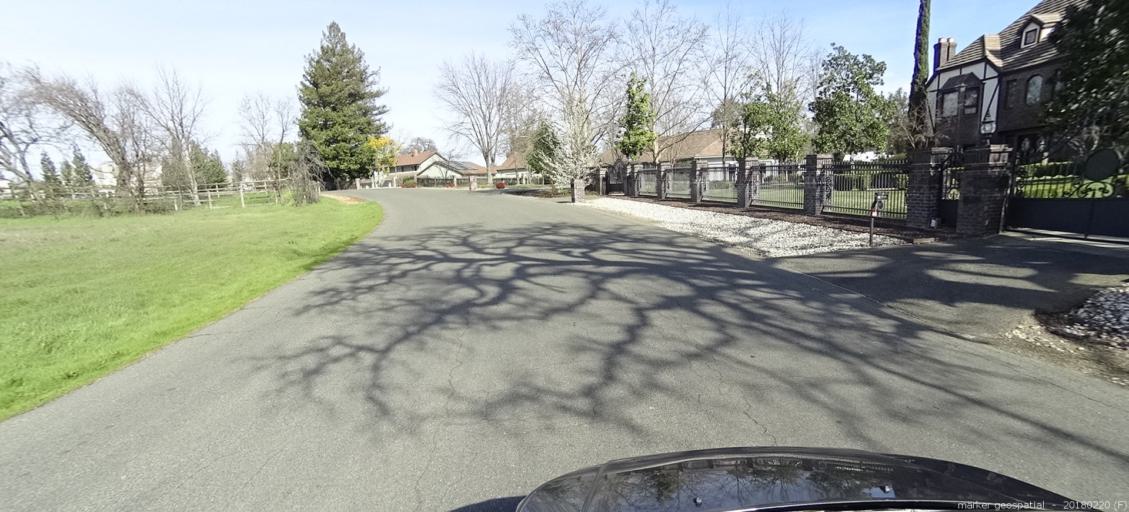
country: US
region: California
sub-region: Sacramento County
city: Orangevale
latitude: 38.7099
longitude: -121.2322
